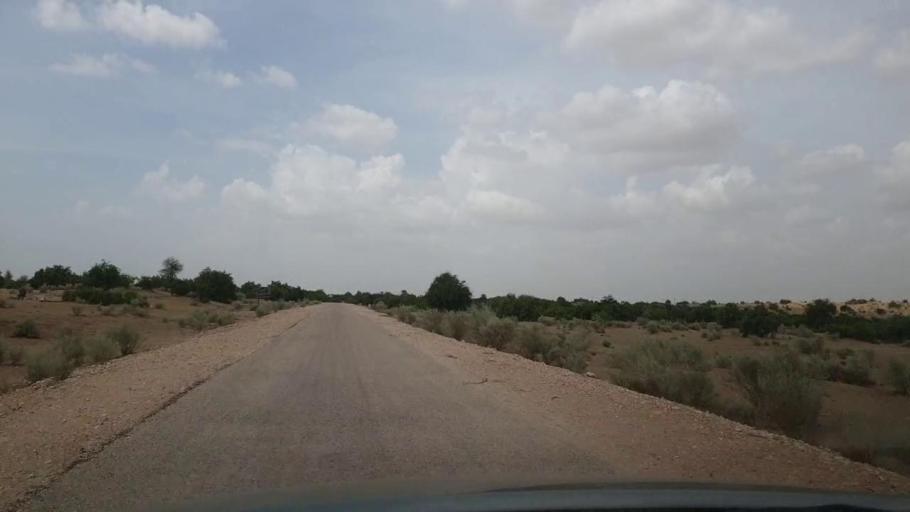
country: PK
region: Sindh
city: Kot Diji
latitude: 27.2167
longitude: 69.0837
